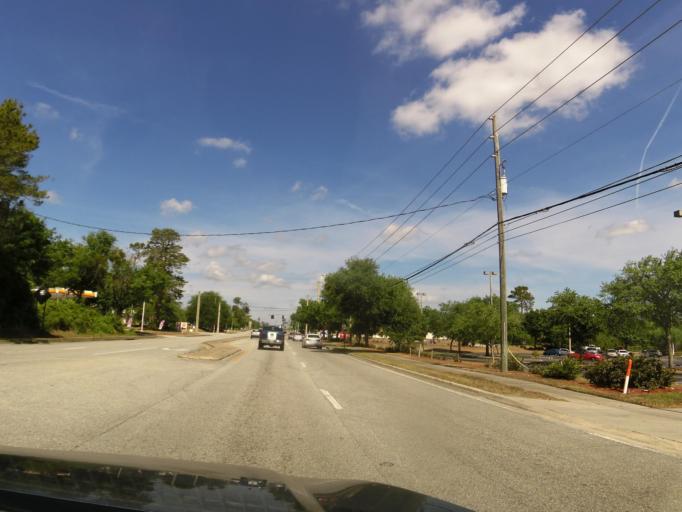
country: US
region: Florida
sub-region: Volusia County
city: Lake Helen
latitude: 28.9438
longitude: -81.2251
